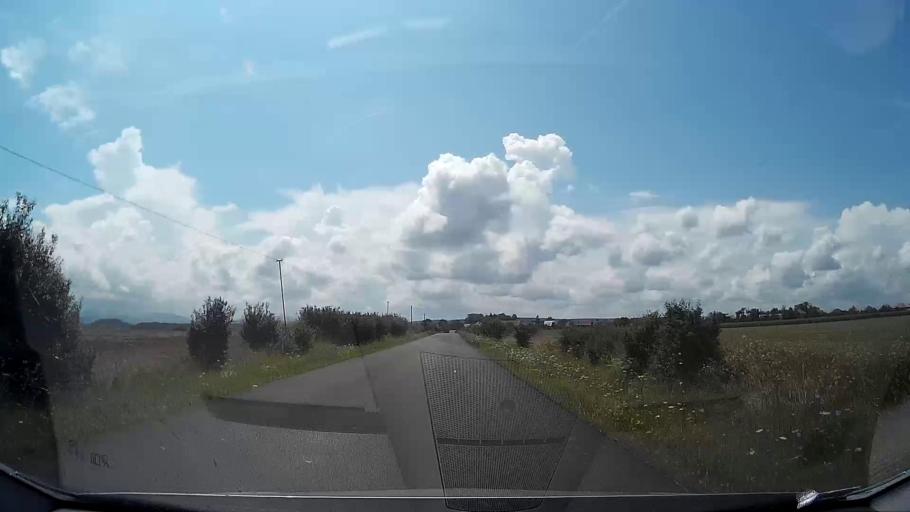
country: SK
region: Banskobystricky
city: Fil'akovo
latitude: 48.3133
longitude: 19.8055
